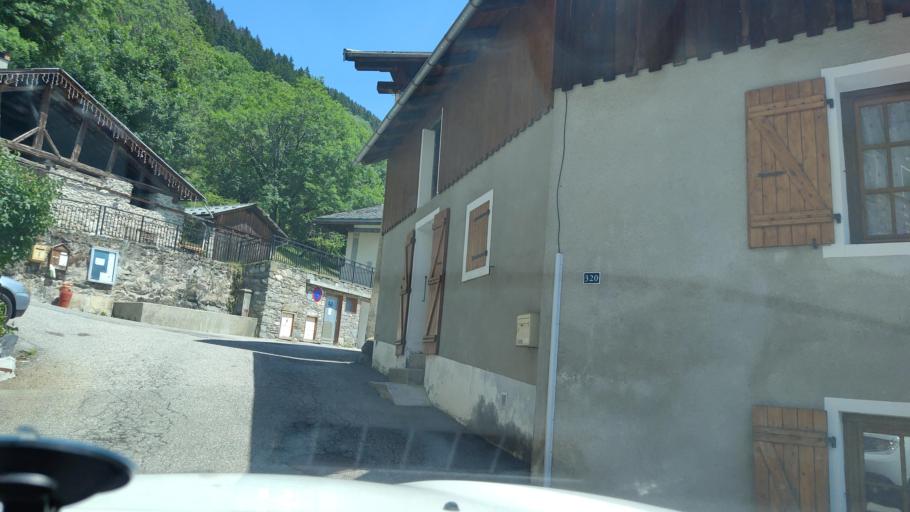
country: FR
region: Rhone-Alpes
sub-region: Departement de la Savoie
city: Bozel
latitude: 45.4517
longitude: 6.6561
